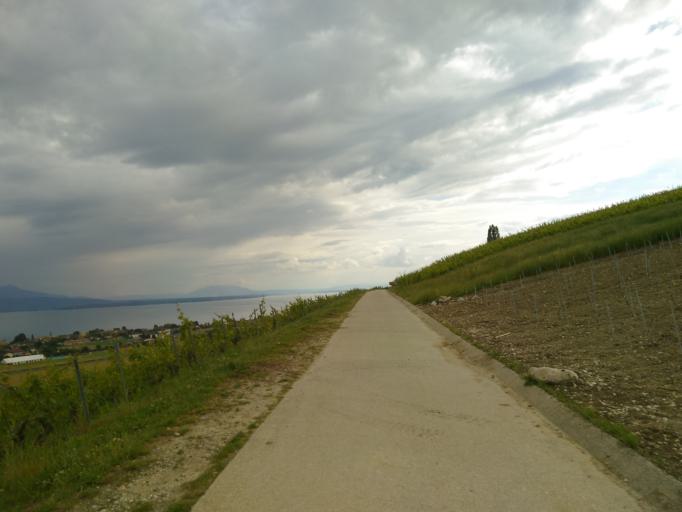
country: CH
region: Vaud
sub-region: Nyon District
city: Perroy
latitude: 46.4821
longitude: 6.3674
